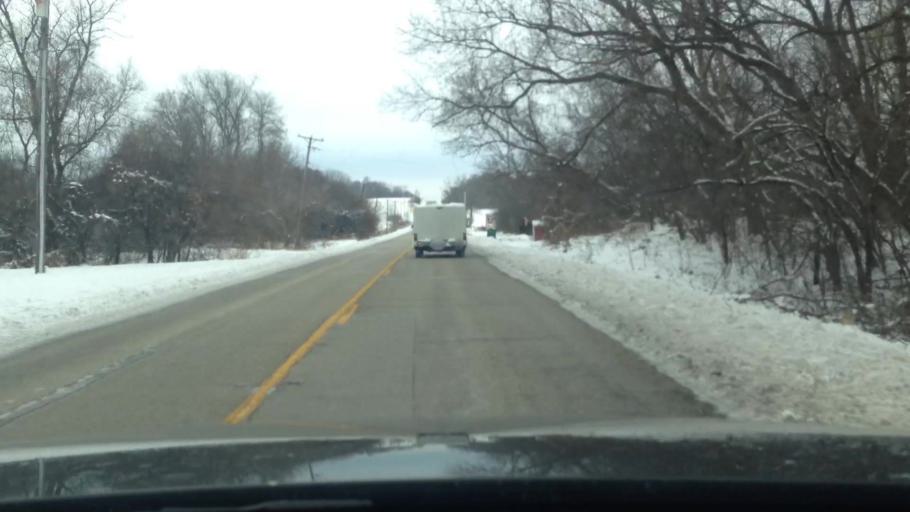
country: US
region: Illinois
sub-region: McHenry County
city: Hebron
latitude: 42.4844
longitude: -88.4425
